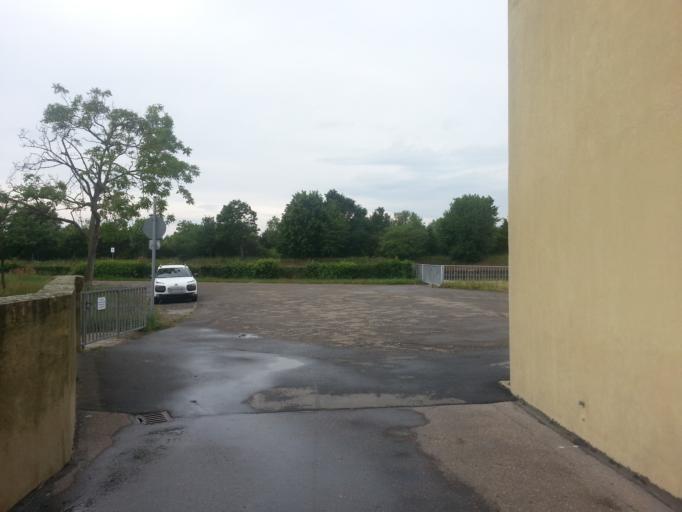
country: DE
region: Baden-Wuerttemberg
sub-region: Karlsruhe Region
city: Ilvesheim
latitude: 49.4780
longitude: 8.5346
